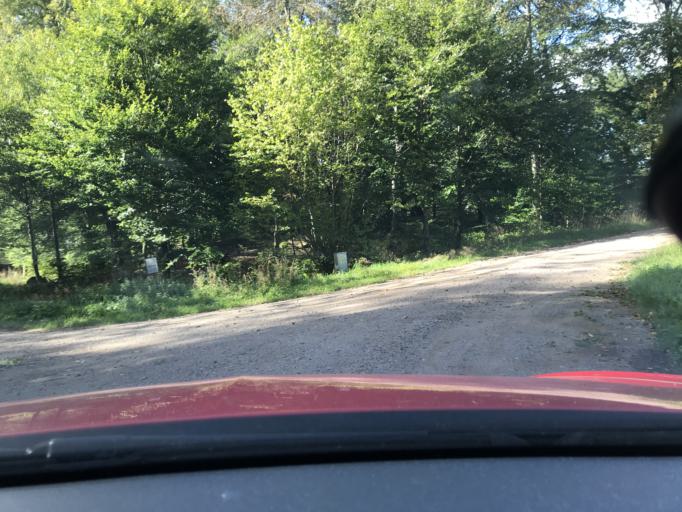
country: SE
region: Skane
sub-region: Hassleholms Kommun
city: Sosdala
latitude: 55.9985
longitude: 13.7052
